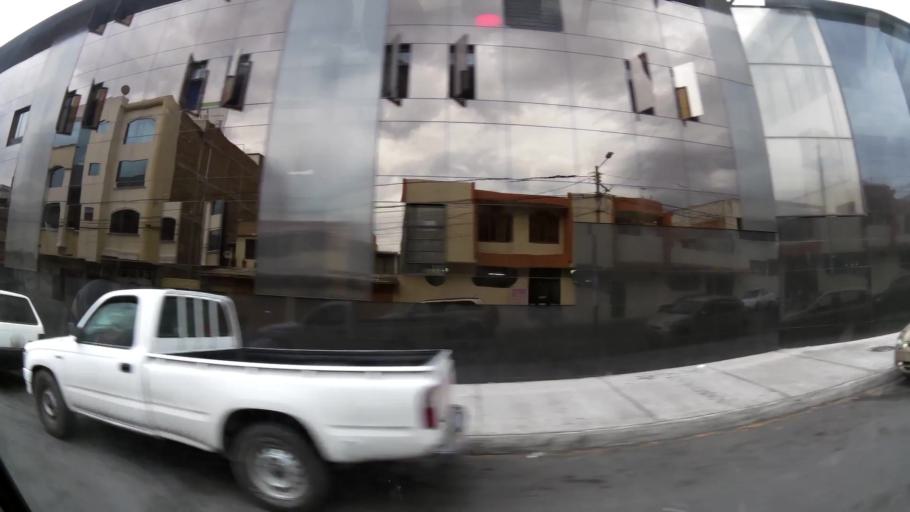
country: EC
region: Tungurahua
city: Ambato
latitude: -1.2342
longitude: -78.6160
